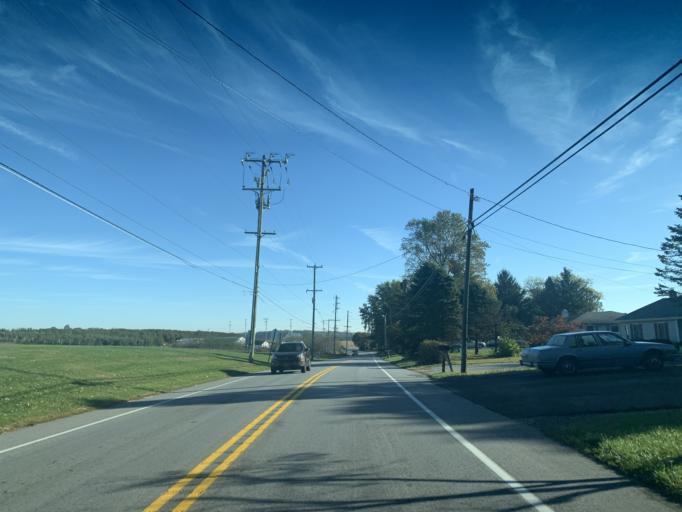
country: US
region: Pennsylvania
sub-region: Chester County
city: Parkesburg
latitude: 39.8940
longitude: -75.9179
